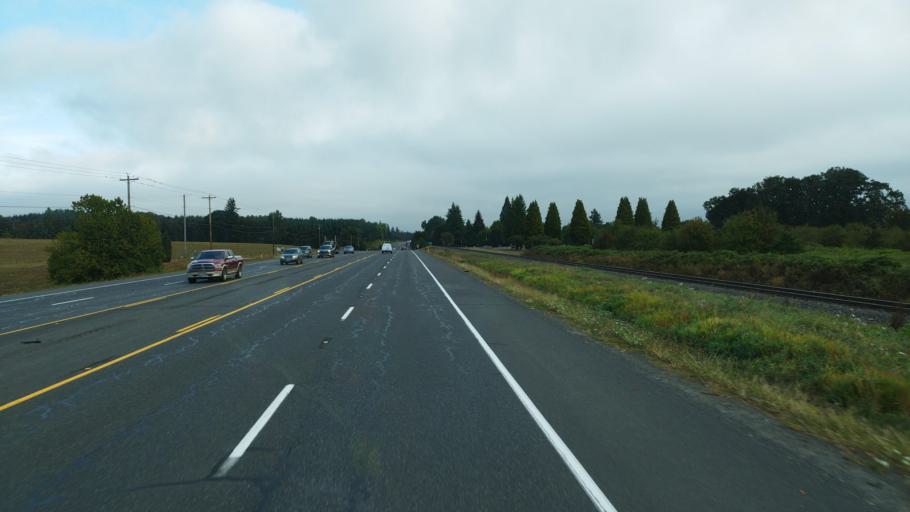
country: US
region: Oregon
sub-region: Columbia County
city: Scappoose
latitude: 45.7839
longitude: -122.8733
